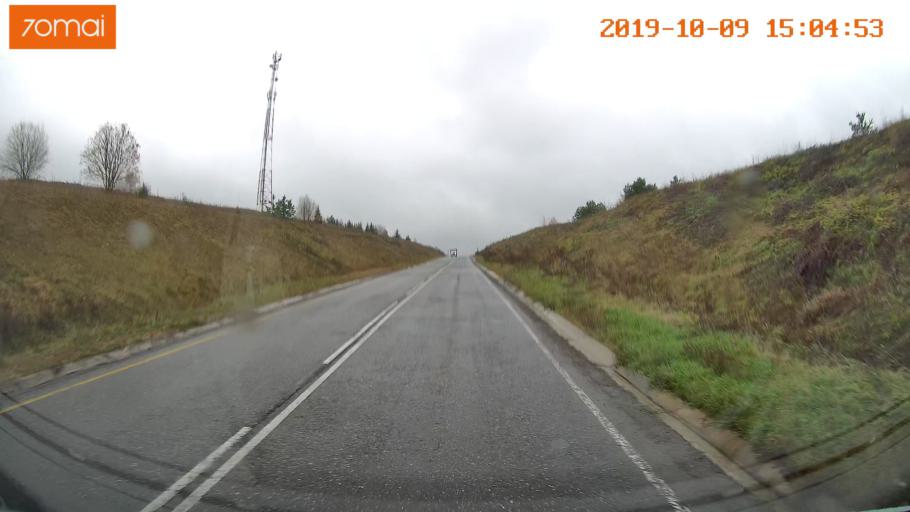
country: RU
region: Kostroma
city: Chistyye Bory
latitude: 58.2528
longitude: 41.6641
